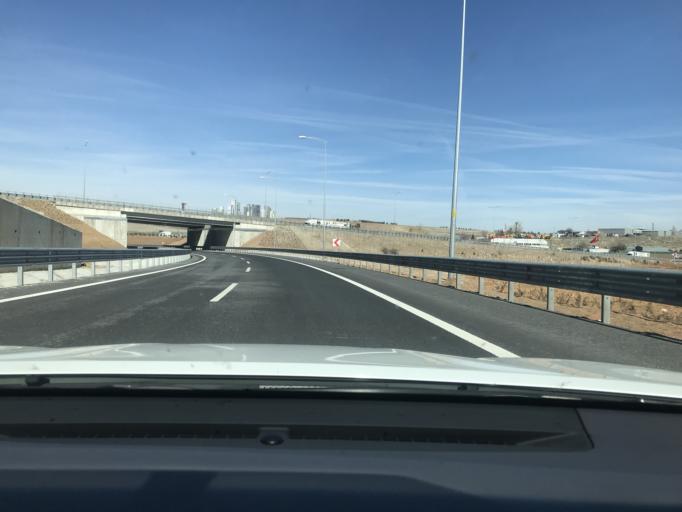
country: TR
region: Ankara
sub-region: Goelbasi
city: Golbasi
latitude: 39.7859
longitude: 32.7471
